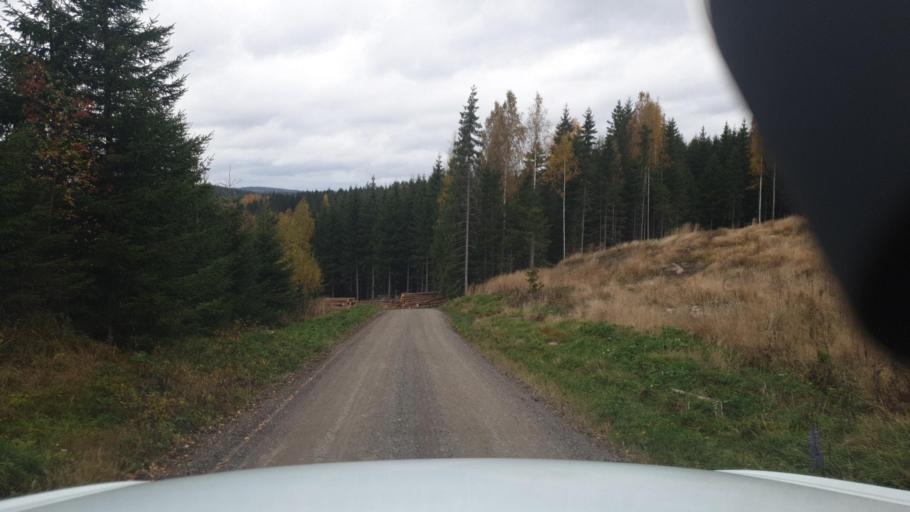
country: SE
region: Vaermland
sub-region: Torsby Kommun
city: Torsby
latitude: 59.9538
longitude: 12.7433
